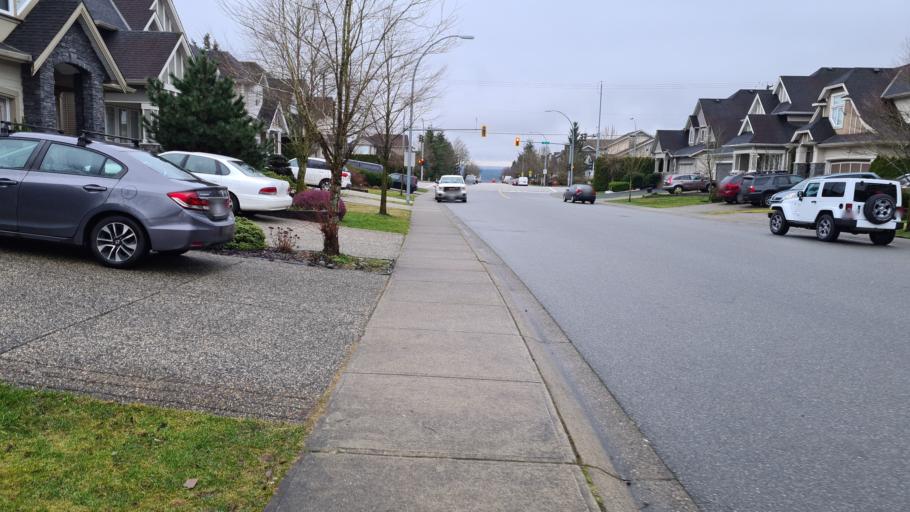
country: CA
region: British Columbia
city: Langley
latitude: 49.1345
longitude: -122.6646
